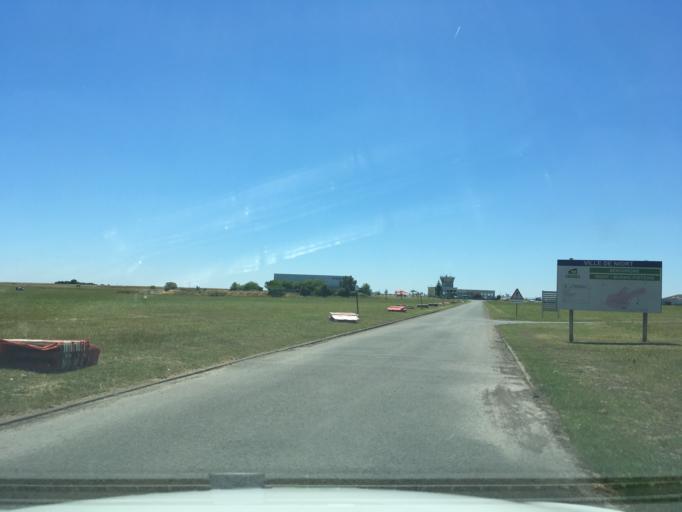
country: FR
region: Poitou-Charentes
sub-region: Departement des Deux-Sevres
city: Vouille
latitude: 46.3181
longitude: -0.3995
